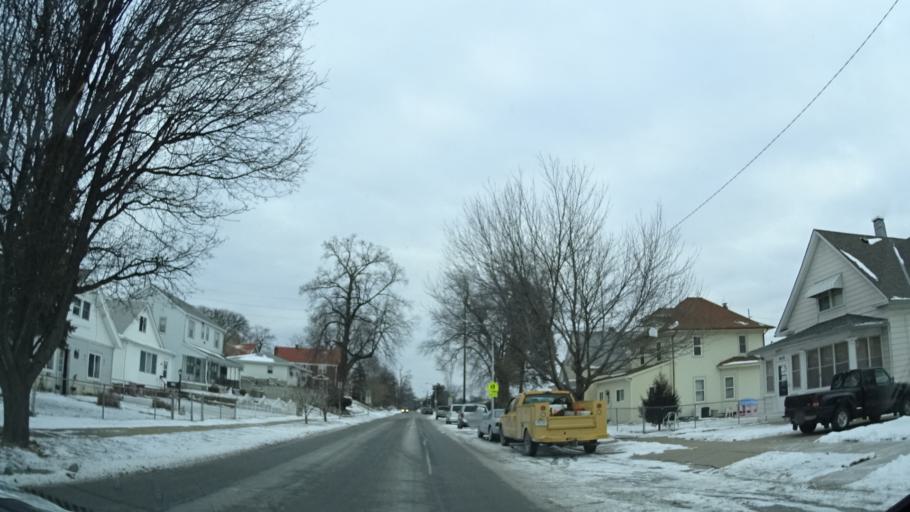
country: US
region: Nebraska
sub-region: Douglas County
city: Omaha
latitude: 41.2152
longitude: -95.9418
